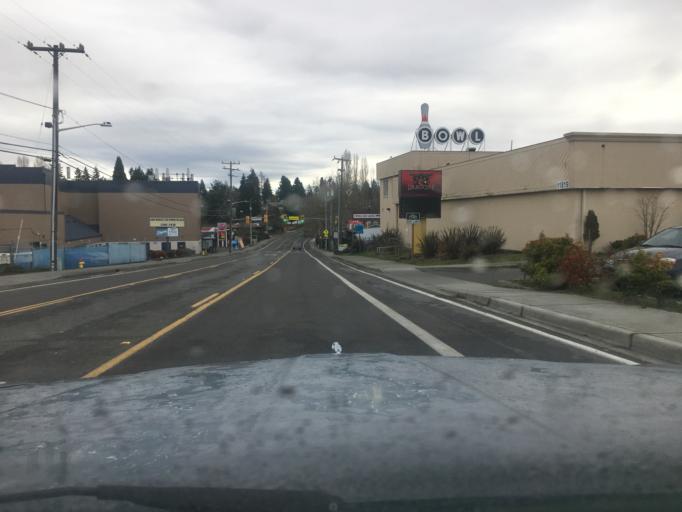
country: US
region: Washington
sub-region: King County
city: Bryn Mawr-Skyway
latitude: 47.4971
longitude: -122.2469
